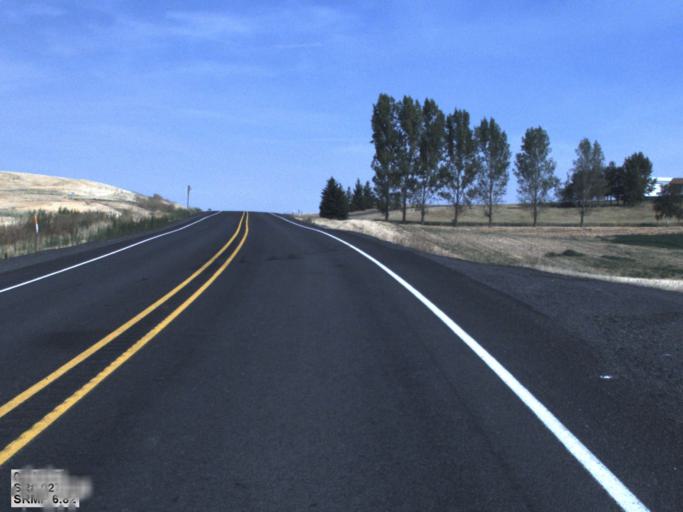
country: US
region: Washington
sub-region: Whitman County
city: Pullman
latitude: 46.8139
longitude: -117.1170
